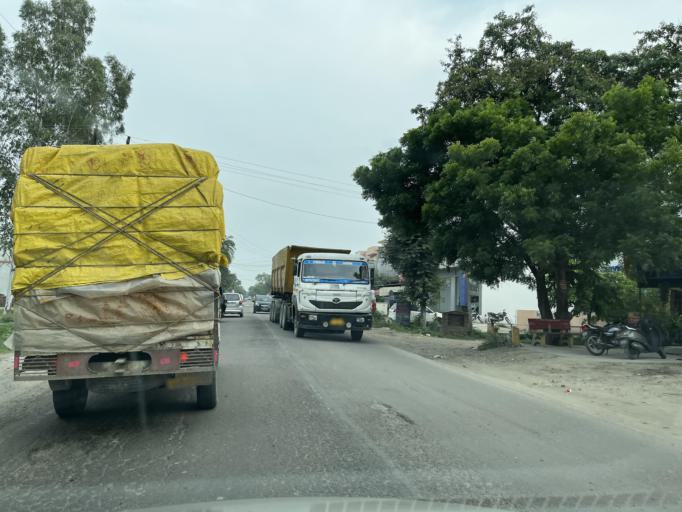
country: IN
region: Uttar Pradesh
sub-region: Rampur
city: Bilaspur
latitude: 29.0368
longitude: 79.2550
